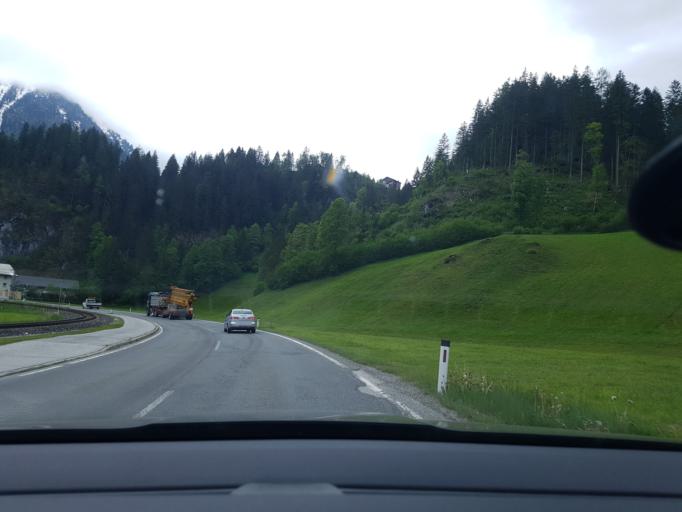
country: AT
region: Salzburg
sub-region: Politischer Bezirk Zell am See
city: Krimml
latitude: 47.2367
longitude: 12.1957
